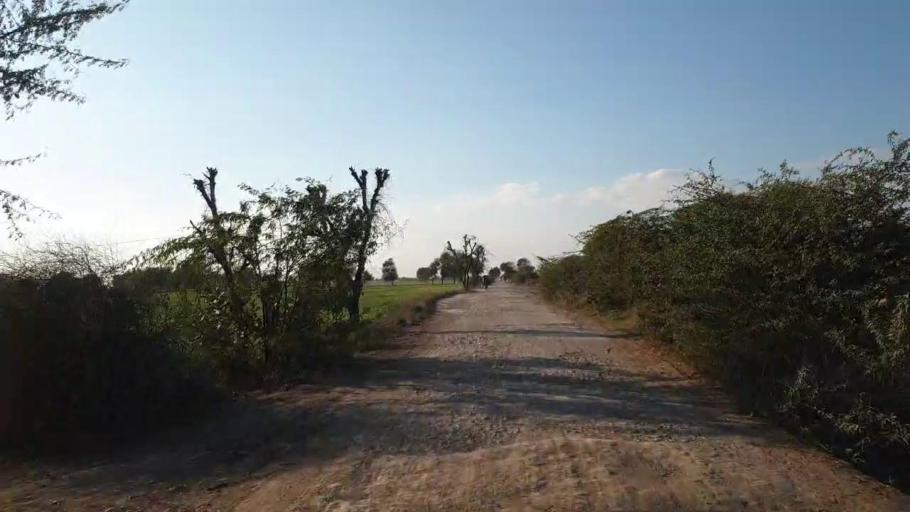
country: PK
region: Sindh
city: Shahpur Chakar
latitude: 26.1372
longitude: 68.5575
